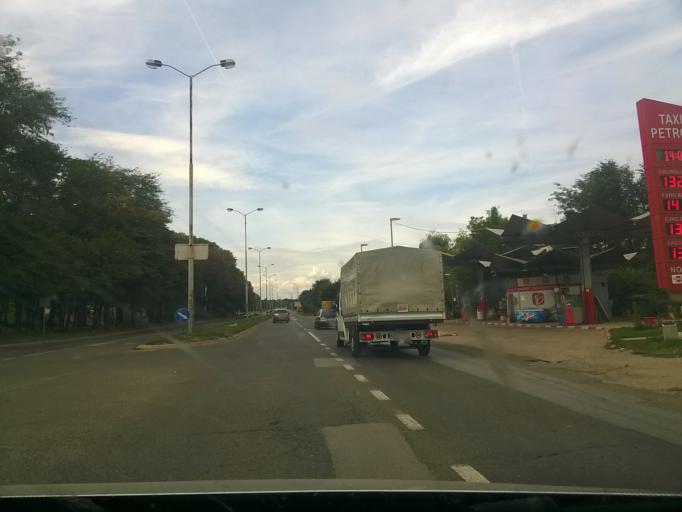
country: RS
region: Autonomna Pokrajina Vojvodina
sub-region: Juznobanatski Okrug
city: Pancevo
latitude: 44.8805
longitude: 20.6550
